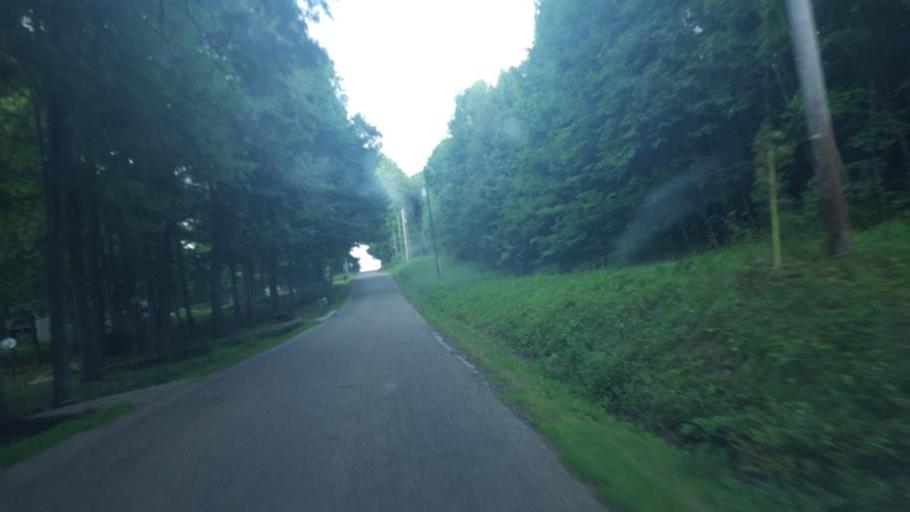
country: US
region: Ohio
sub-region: Sandusky County
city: Bellville
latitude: 40.6511
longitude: -82.5013
